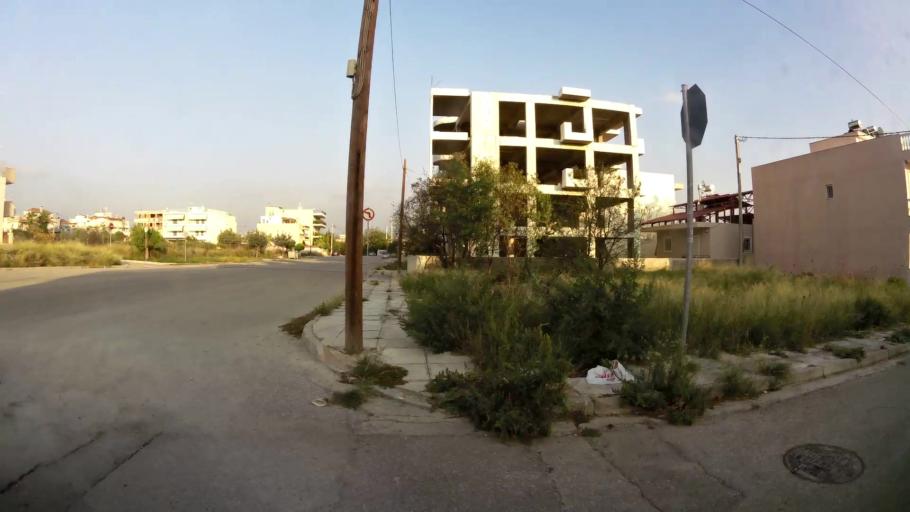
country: GR
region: Attica
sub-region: Nomarchia Anatolikis Attikis
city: Acharnes
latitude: 38.0962
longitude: 23.7421
